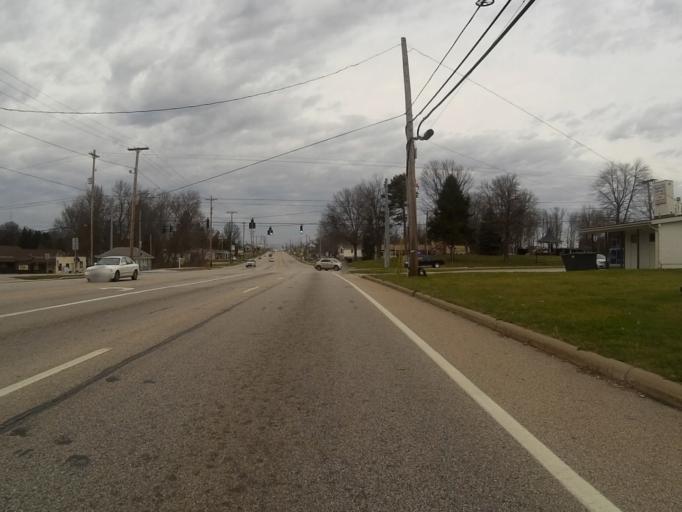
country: US
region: Ohio
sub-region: Portage County
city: Brimfield
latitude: 41.0994
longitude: -81.3460
